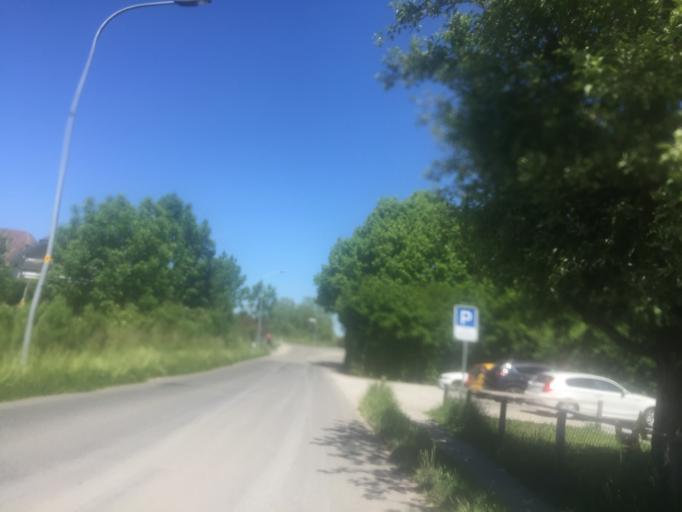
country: CH
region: Bern
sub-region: Thun District
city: Thierachern
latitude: 46.7504
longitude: 7.5646
